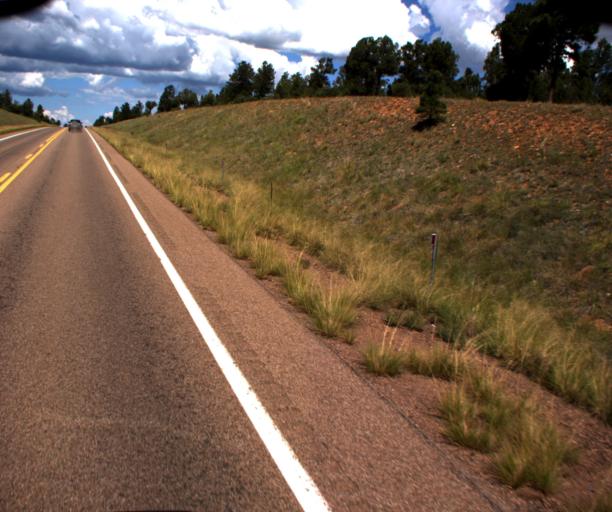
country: US
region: Arizona
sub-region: Navajo County
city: Heber-Overgaard
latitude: 34.3738
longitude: -110.4606
